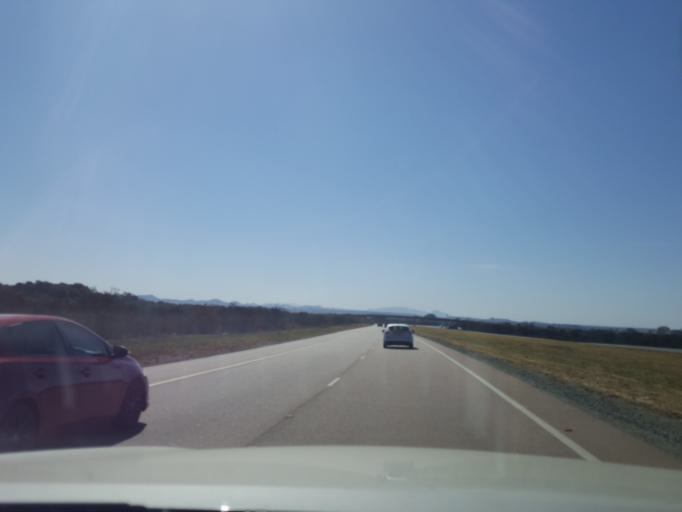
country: ZA
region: North-West
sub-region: Bojanala Platinum District Municipality
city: Brits
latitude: -25.7439
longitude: 27.5312
